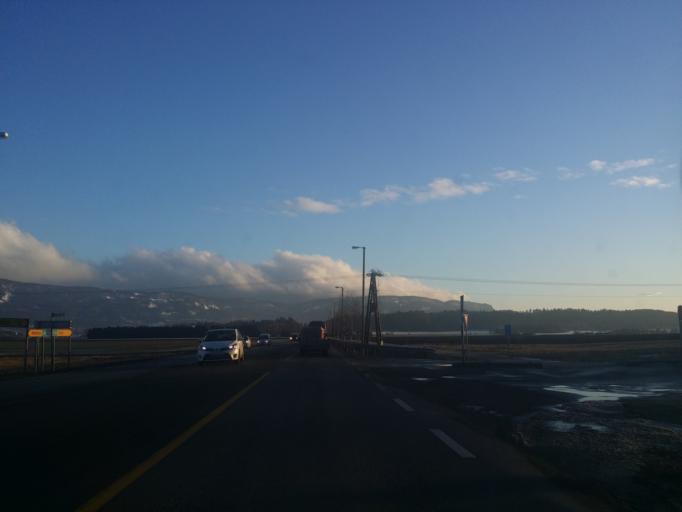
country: NO
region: Buskerud
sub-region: Hole
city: Vik
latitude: 60.1152
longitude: 10.2829
